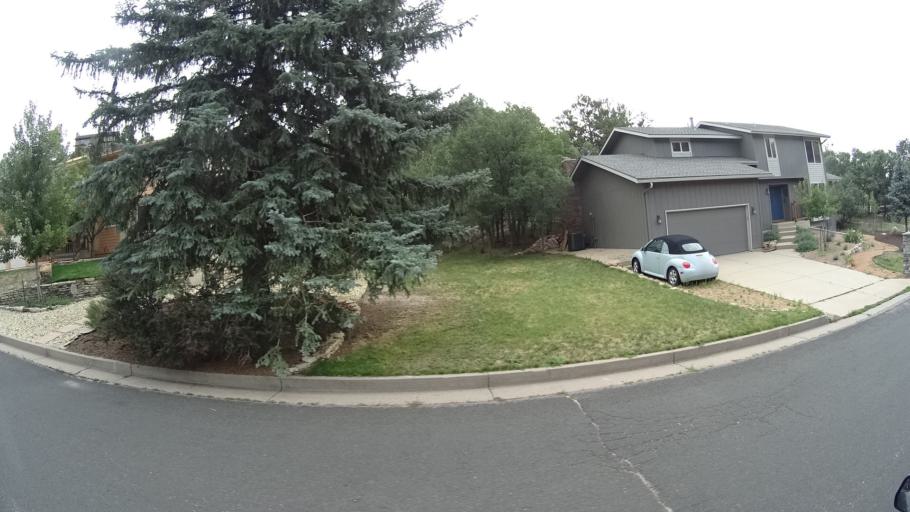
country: US
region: Colorado
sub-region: El Paso County
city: Air Force Academy
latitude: 38.9345
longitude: -104.8595
